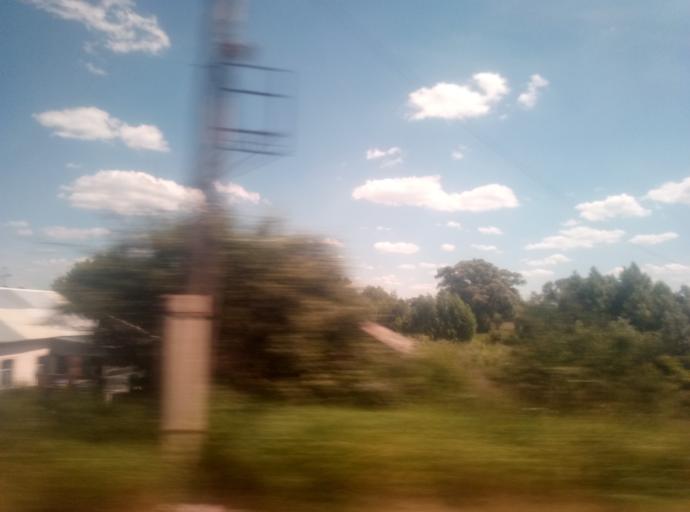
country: RU
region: Tula
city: Kireyevsk
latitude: 53.9739
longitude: 37.9299
